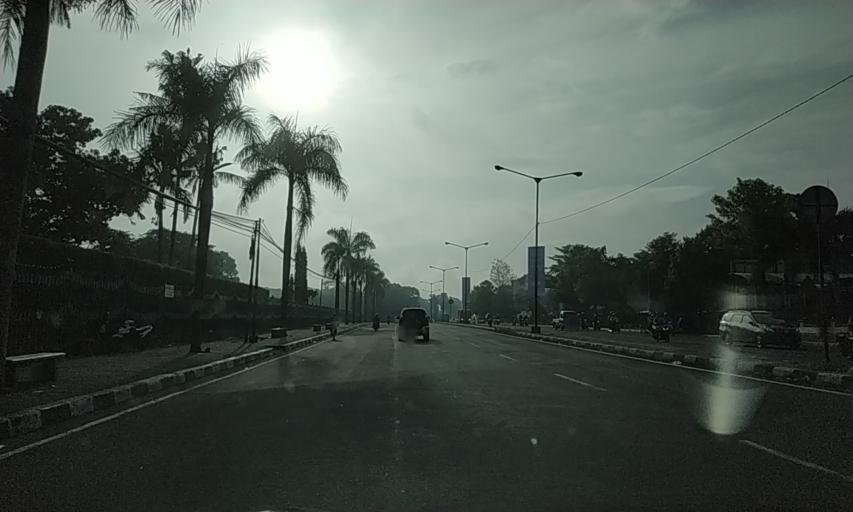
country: ID
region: Central Java
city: Candi Prambanan
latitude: -7.7554
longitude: 110.4894
